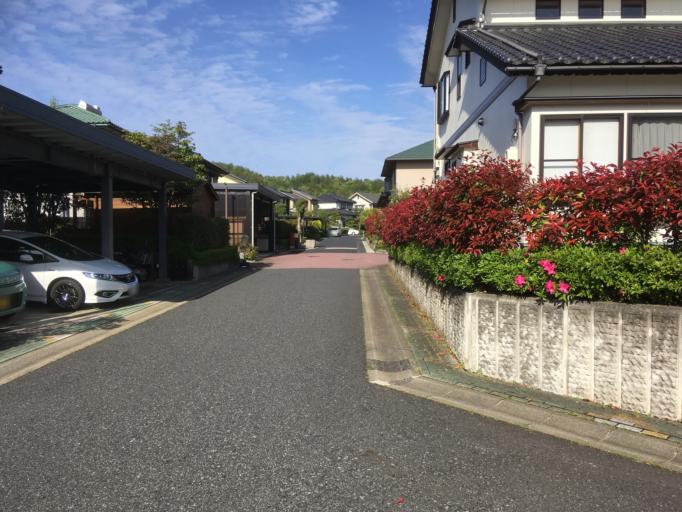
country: JP
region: Tottori
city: Tottori
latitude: 35.4515
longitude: 134.2639
